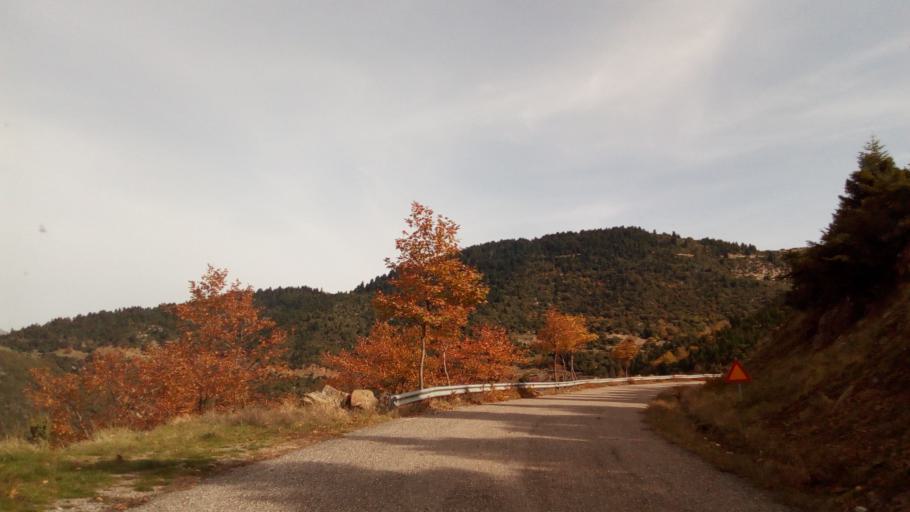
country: GR
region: West Greece
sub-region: Nomos Aitolias kai Akarnanias
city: Thermo
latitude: 38.5569
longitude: 21.8169
